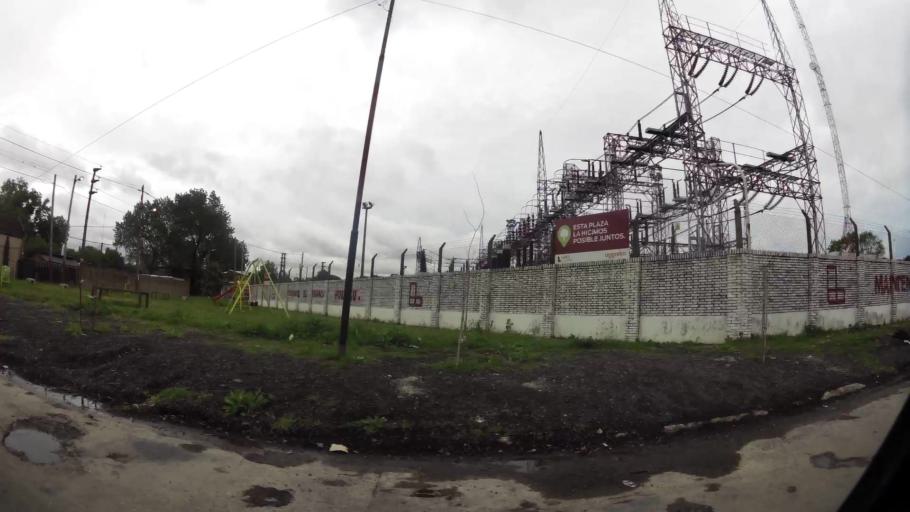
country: AR
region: Buenos Aires
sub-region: Partido de Lanus
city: Lanus
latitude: -34.7217
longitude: -58.3880
